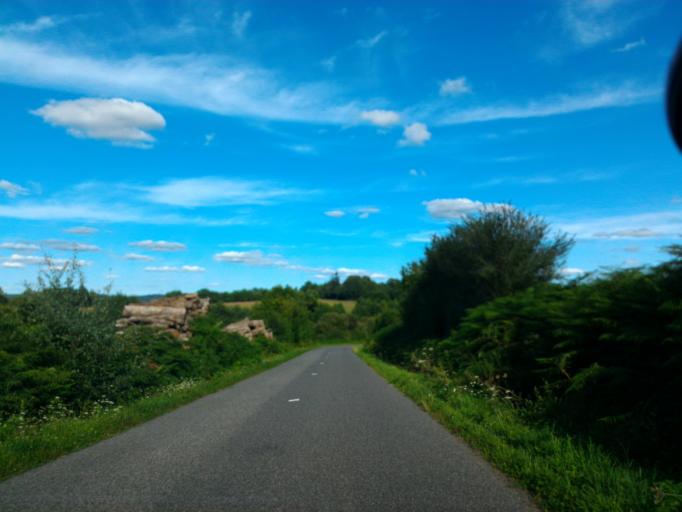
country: FR
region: Poitou-Charentes
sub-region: Departement de la Charente
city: Brigueuil
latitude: 45.9982
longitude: 0.8646
